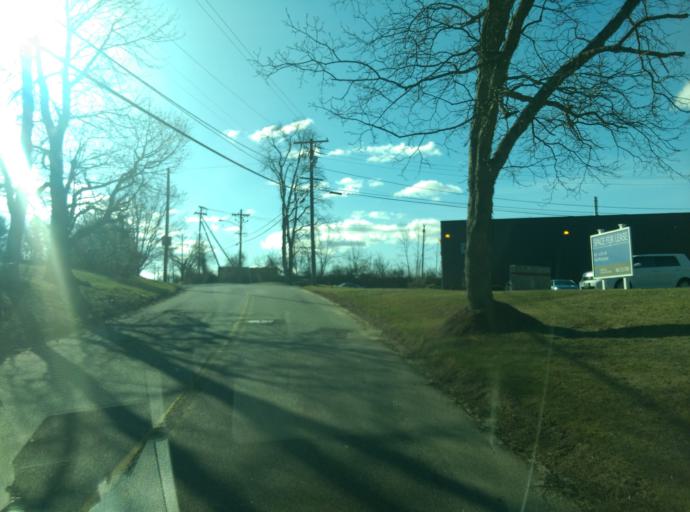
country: US
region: Massachusetts
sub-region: Essex County
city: Haverhill
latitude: 42.7559
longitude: -71.1217
